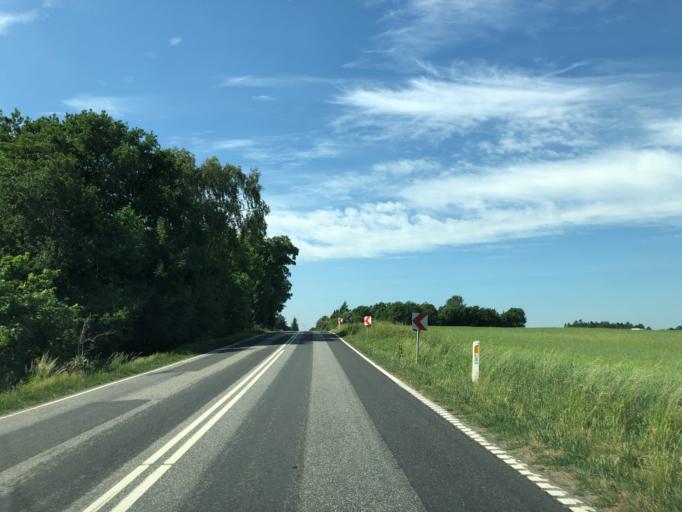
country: DK
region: South Denmark
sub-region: Vejle Kommune
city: Give
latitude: 55.8855
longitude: 9.2197
